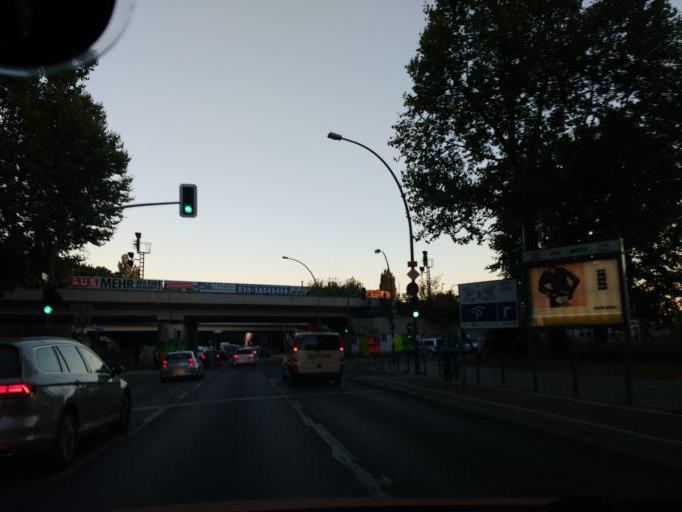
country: DE
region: Berlin
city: Treptow Bezirk
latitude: 52.4910
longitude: 13.4587
